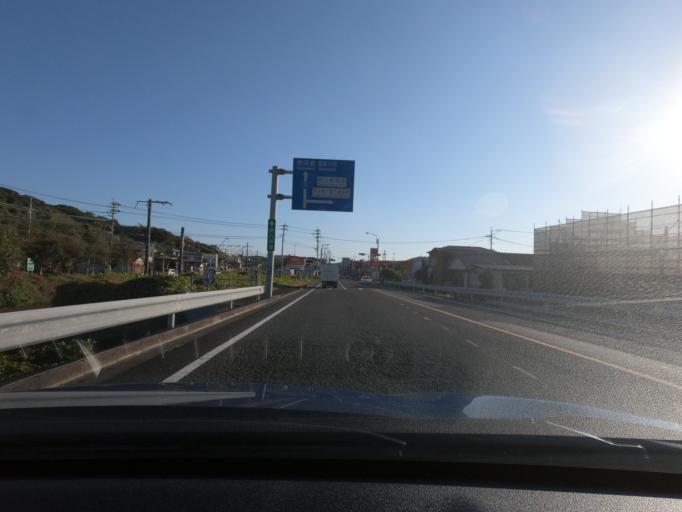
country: JP
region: Kagoshima
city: Akune
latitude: 32.0261
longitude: 130.1957
